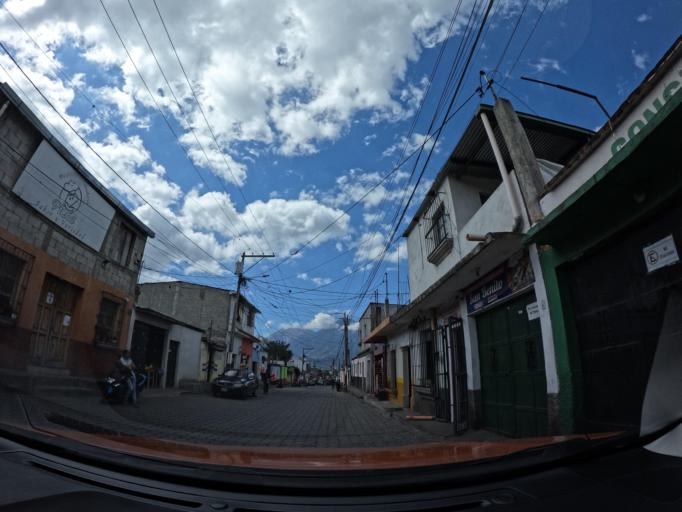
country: GT
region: Sacatepequez
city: Ciudad Vieja
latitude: 14.5262
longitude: -90.7524
